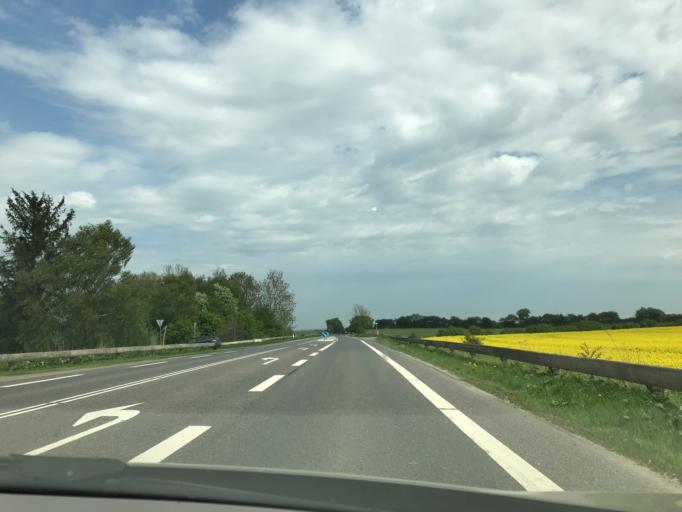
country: DK
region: South Denmark
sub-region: Assens Kommune
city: Assens
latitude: 55.2870
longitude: 9.9251
